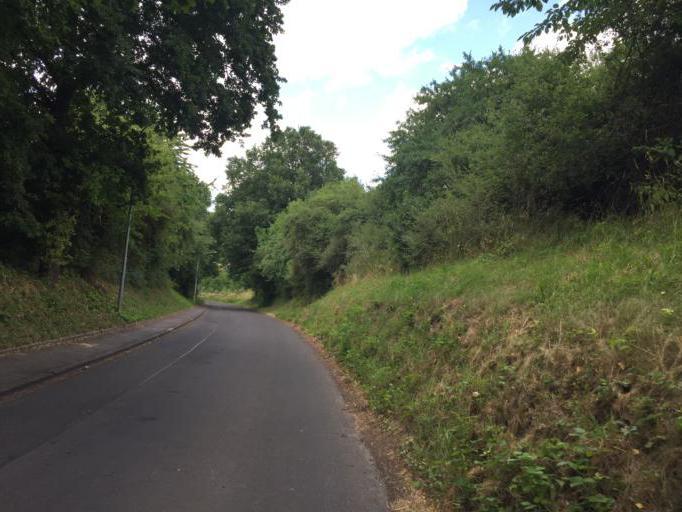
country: DE
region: Hesse
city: Lollar
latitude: 50.6423
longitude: 8.6774
